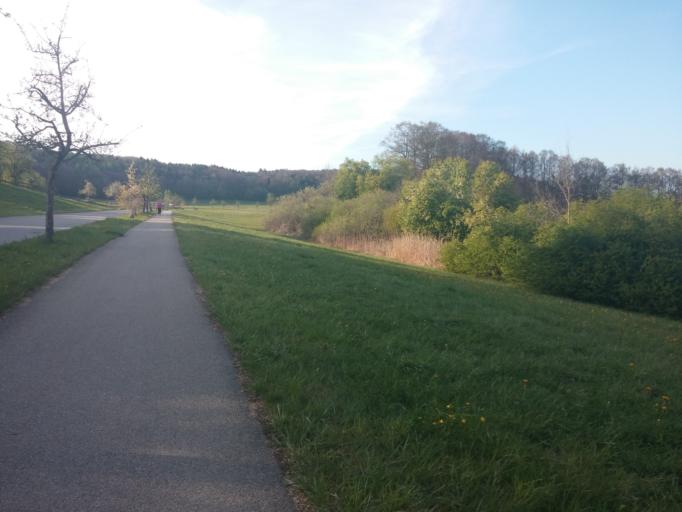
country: DE
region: Baden-Wuerttemberg
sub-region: Tuebingen Region
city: Bad Schussenried
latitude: 48.0015
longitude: 9.6426
